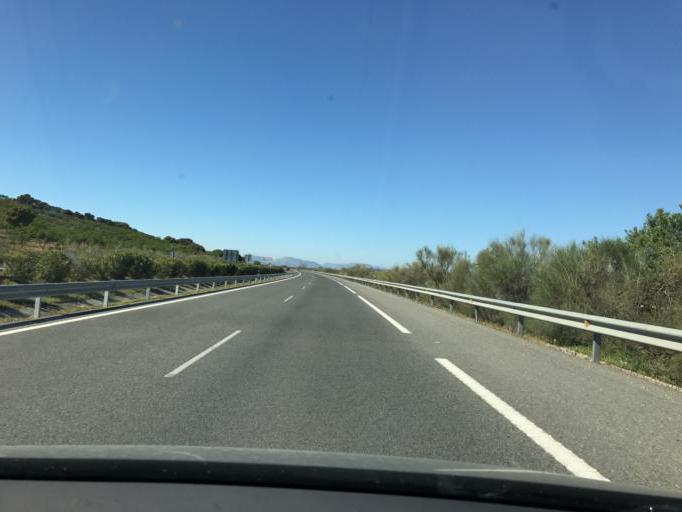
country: ES
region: Andalusia
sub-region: Provincia de Malaga
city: Villanueva de Tapia
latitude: 37.1149
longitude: -4.3022
